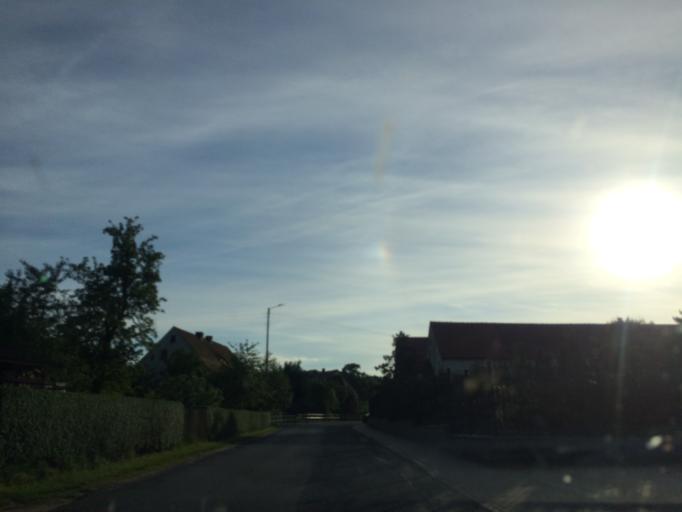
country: PL
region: Lower Silesian Voivodeship
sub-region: Powiat dzierzoniowski
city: Pieszyce
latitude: 50.7514
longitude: 16.5096
